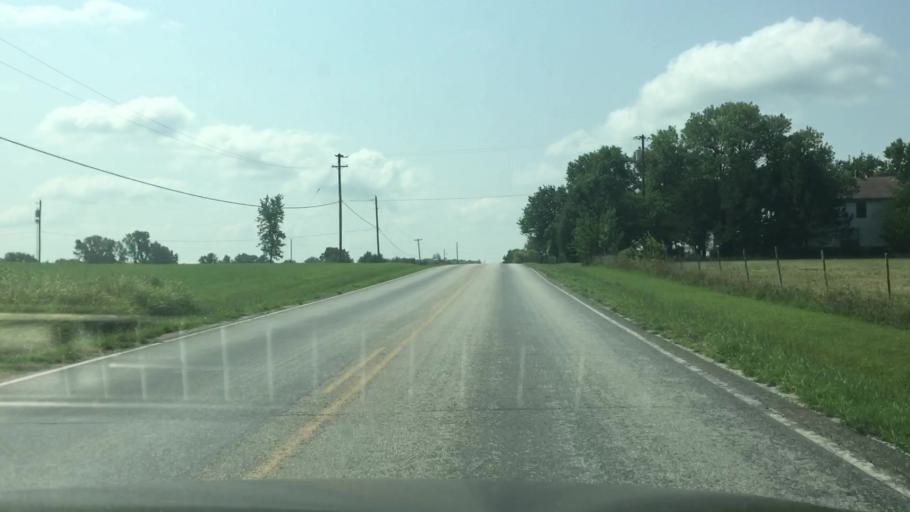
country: US
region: Kansas
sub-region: Allen County
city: Iola
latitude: 37.8977
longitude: -95.4094
